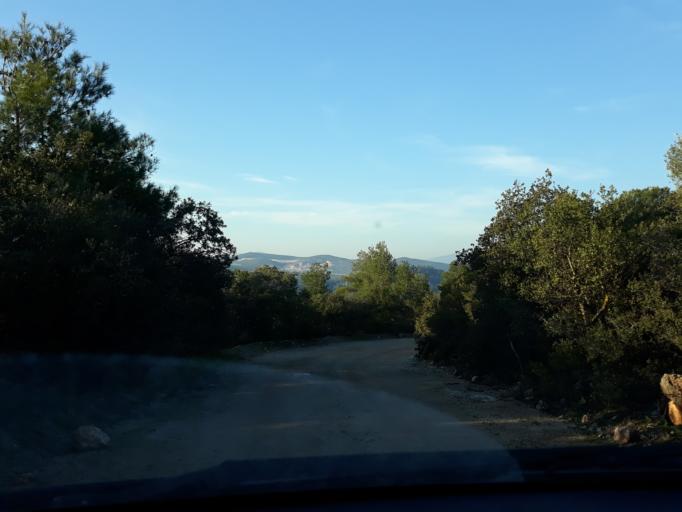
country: GR
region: Central Greece
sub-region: Nomos Voiotias
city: Asopia
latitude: 38.2724
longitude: 23.5329
